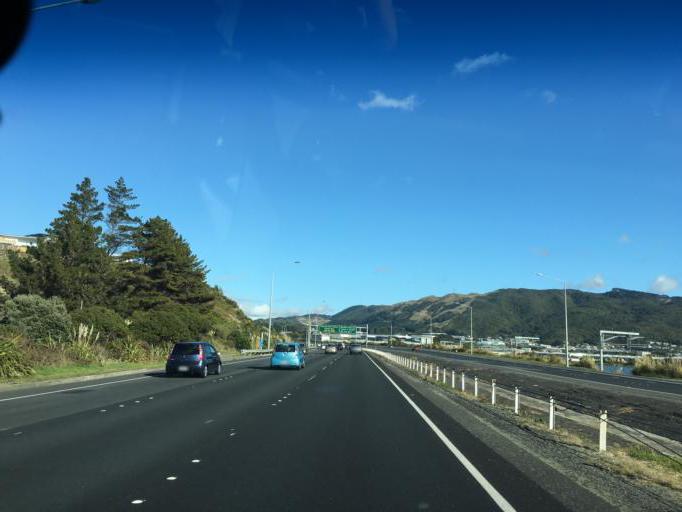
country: NZ
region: Wellington
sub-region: Porirua City
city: Porirua
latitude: -41.1264
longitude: 174.8472
